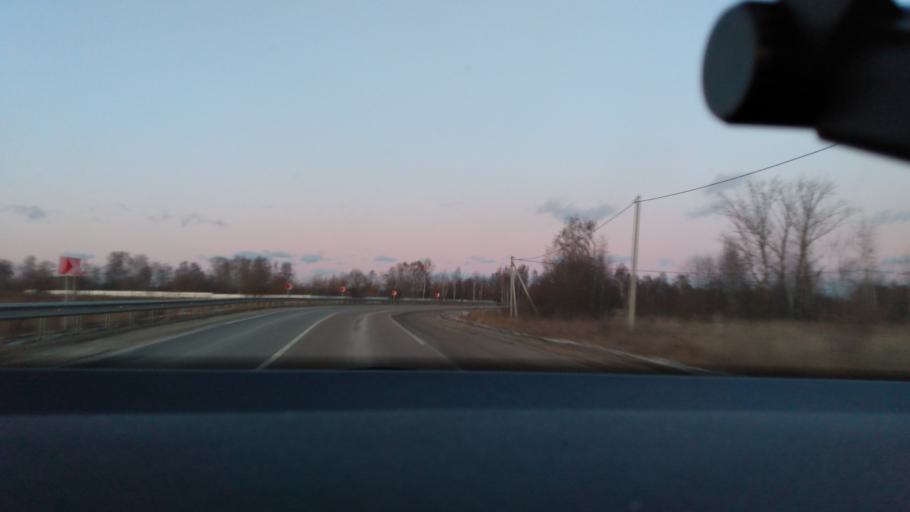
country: RU
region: Moskovskaya
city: Krasnaya Poyma
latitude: 55.1247
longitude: 39.0780
